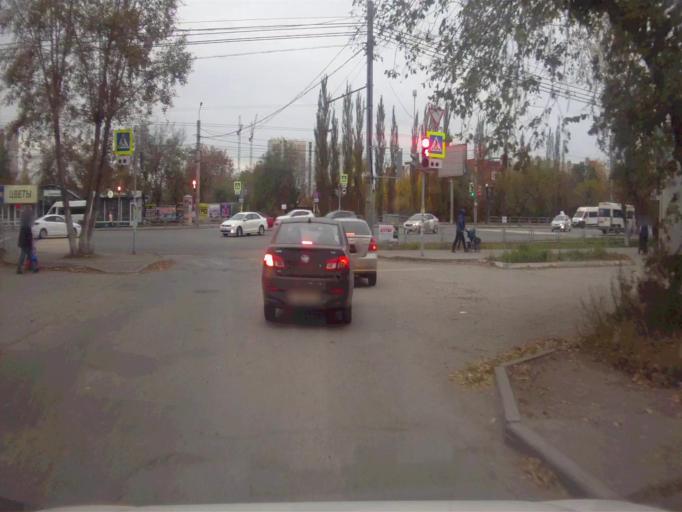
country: RU
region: Chelyabinsk
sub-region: Gorod Chelyabinsk
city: Chelyabinsk
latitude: 55.1792
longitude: 61.3216
